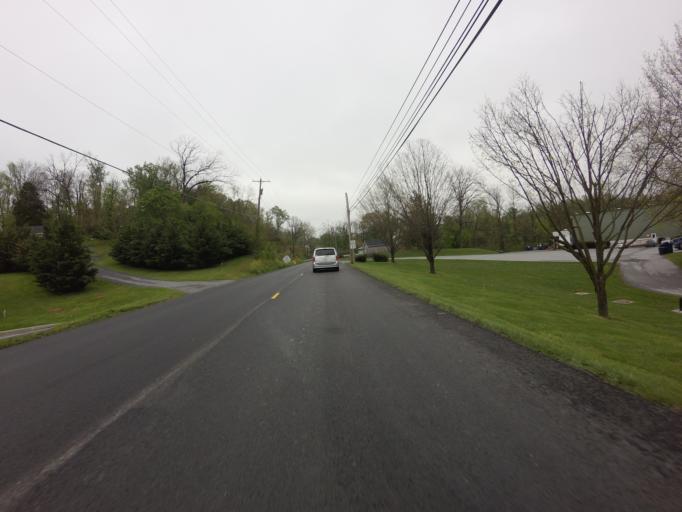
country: US
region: Maryland
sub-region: Carroll County
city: New Windsor
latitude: 39.5391
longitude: -77.1051
